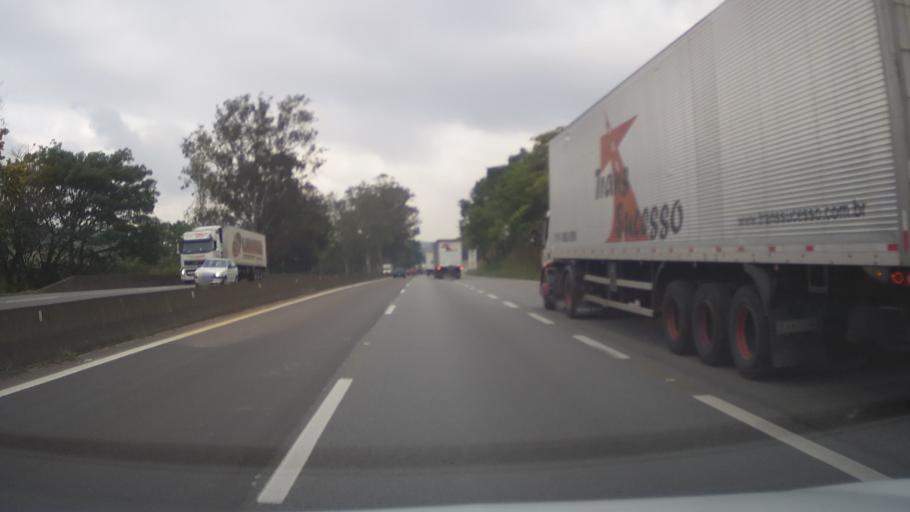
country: BR
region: Minas Gerais
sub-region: Extrema
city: Extrema
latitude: -22.8761
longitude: -46.3685
